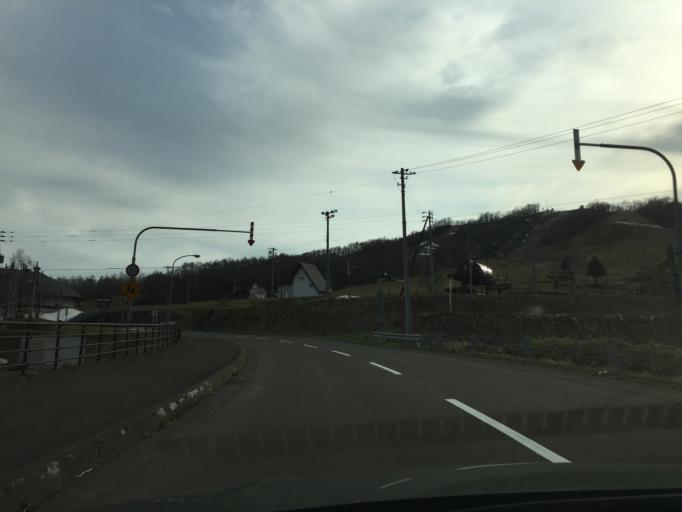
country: JP
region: Hokkaido
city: Utashinai
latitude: 43.5225
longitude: 142.0202
